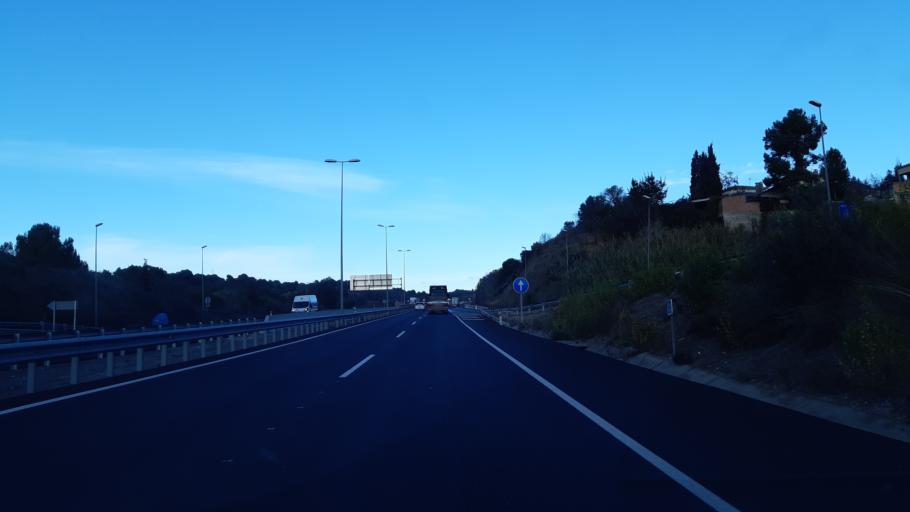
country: ES
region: Catalonia
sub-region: Provincia de Barcelona
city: Esparreguera
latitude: 41.5340
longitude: 1.8638
